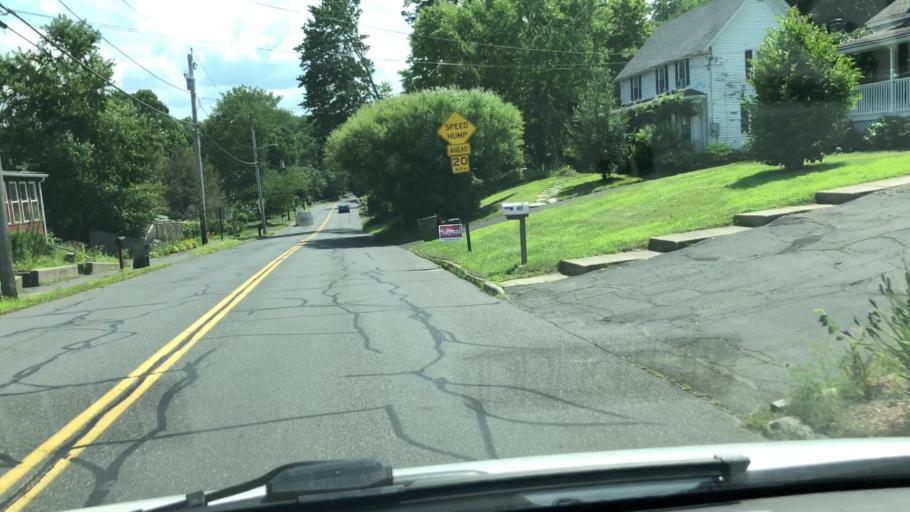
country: US
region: Massachusetts
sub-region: Hampshire County
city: Northampton
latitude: 42.3288
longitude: -72.6775
